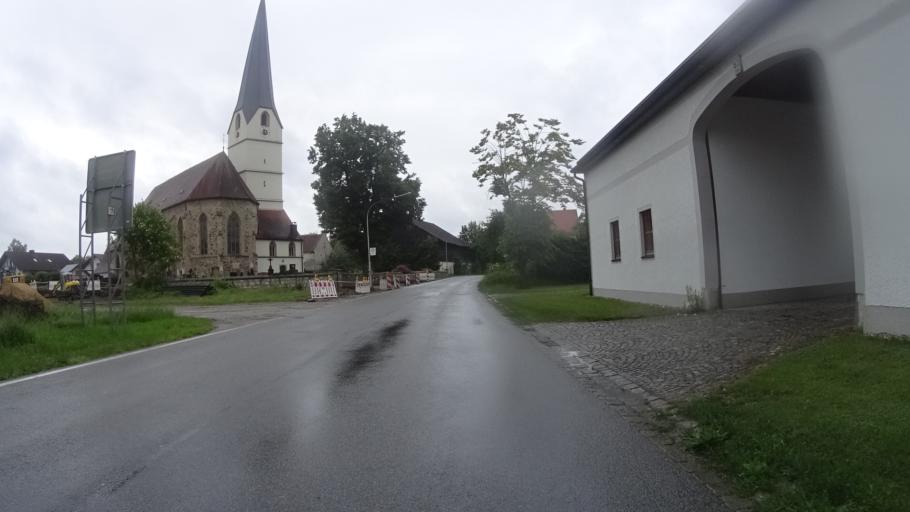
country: AT
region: Upper Austria
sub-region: Politischer Bezirk Scharding
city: Scharding
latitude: 48.4414
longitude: 13.3981
